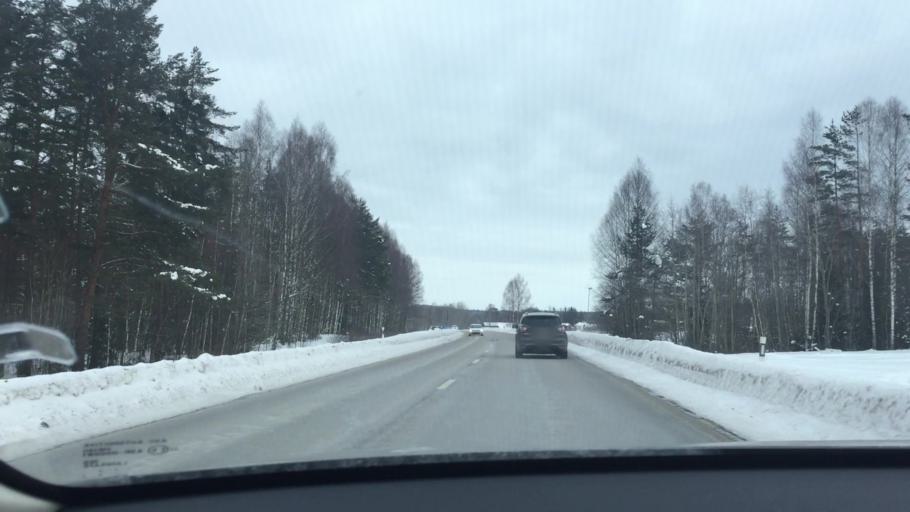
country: SE
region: Dalarna
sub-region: Faluns Kommun
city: Svardsjo
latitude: 60.6394
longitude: 15.8398
